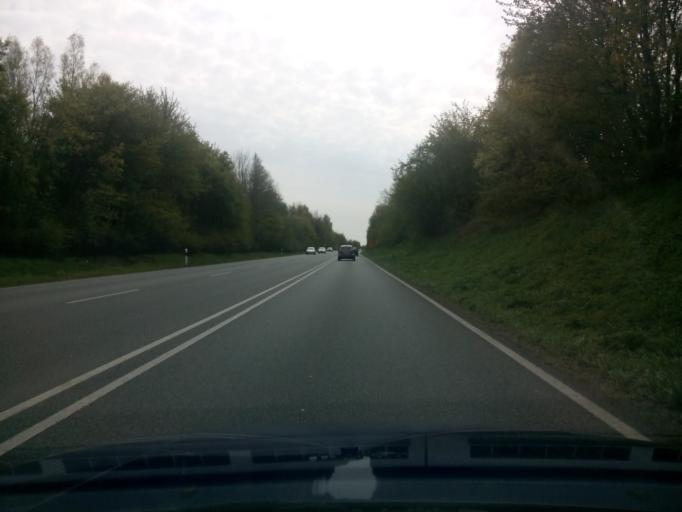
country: DE
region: Lower Saxony
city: Stuhr
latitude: 53.0120
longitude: 8.7985
